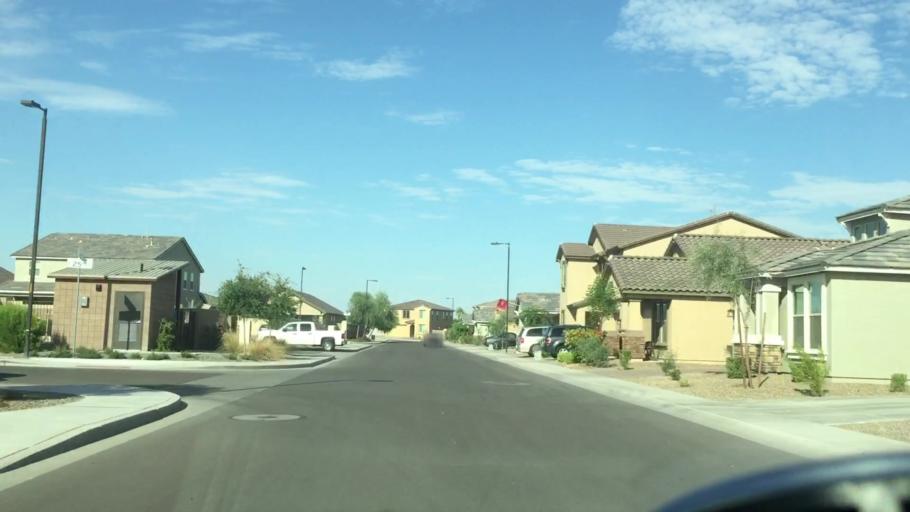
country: US
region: Arizona
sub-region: Maricopa County
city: Guadalupe
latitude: 33.3752
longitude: -112.0288
